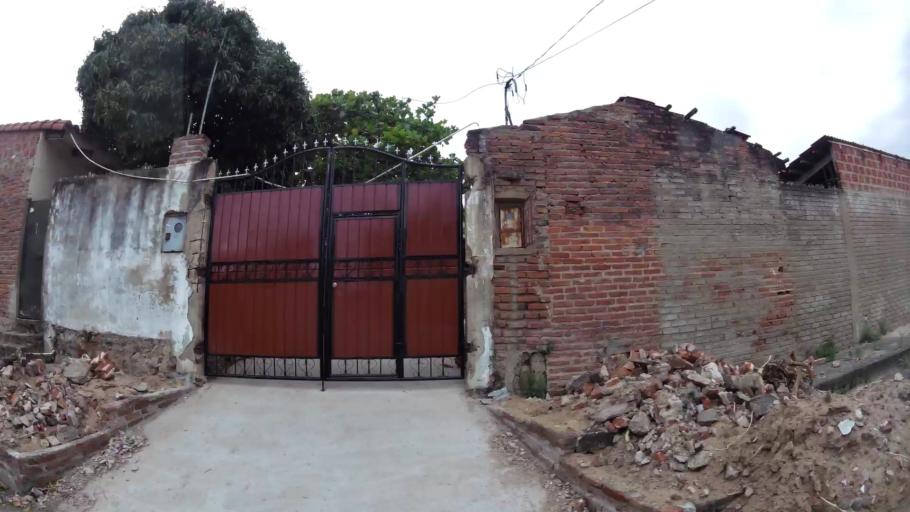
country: BO
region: Santa Cruz
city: Santa Cruz de la Sierra
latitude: -17.7752
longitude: -63.2039
